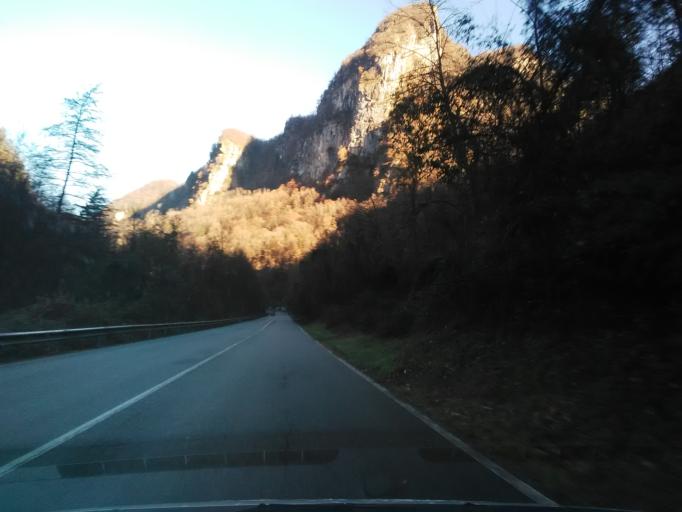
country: IT
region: Piedmont
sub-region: Provincia di Vercelli
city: Varallo
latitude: 45.8006
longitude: 8.2728
